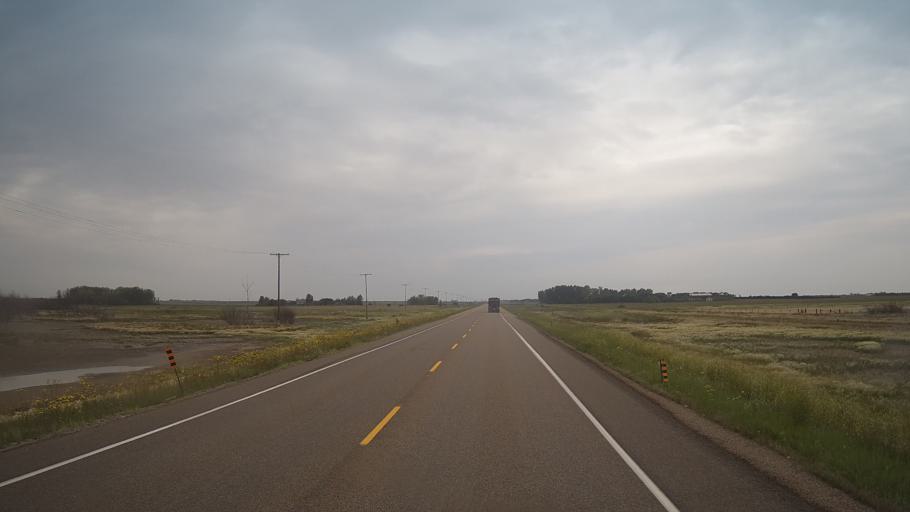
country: CA
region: Saskatchewan
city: Langham
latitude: 52.1289
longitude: -107.1320
